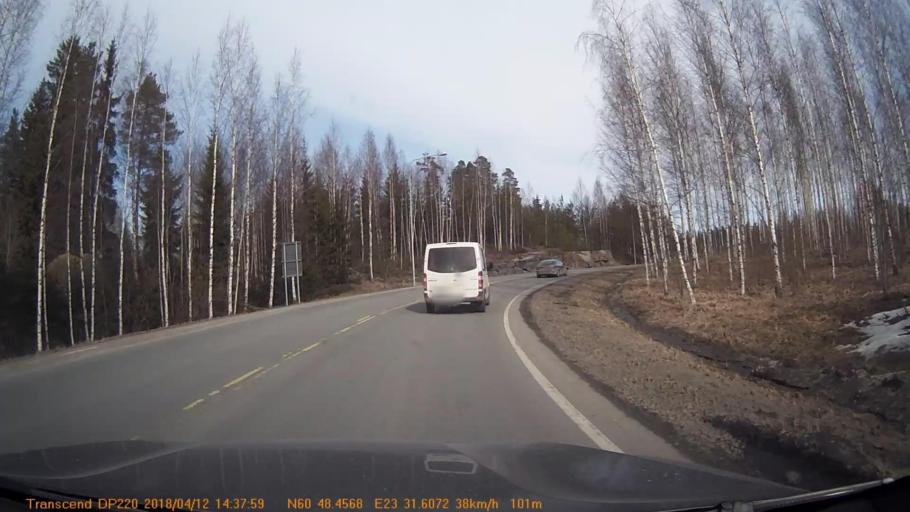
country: FI
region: Haeme
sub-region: Forssa
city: Jokioinen
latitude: 60.8078
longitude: 23.5281
